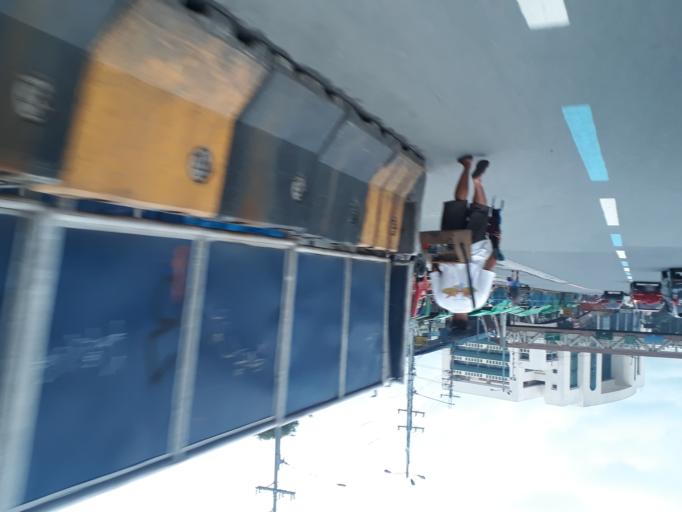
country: PH
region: Calabarzon
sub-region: Province of Rizal
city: San Mateo
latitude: 14.6855
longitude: 121.0868
